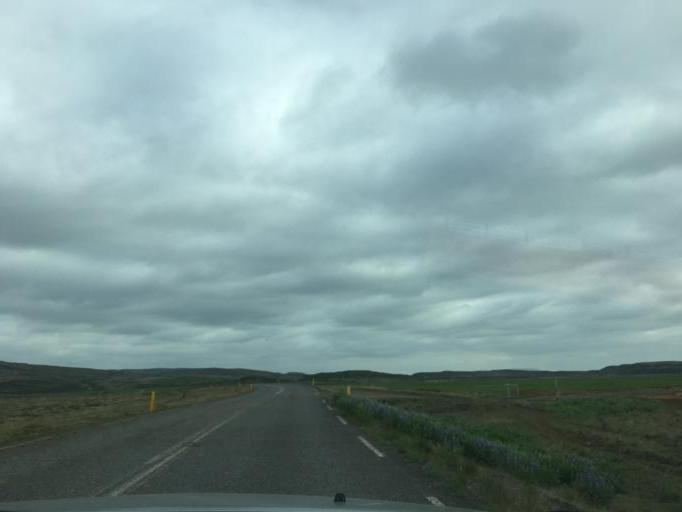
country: IS
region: South
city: Vestmannaeyjar
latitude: 64.2717
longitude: -20.2261
